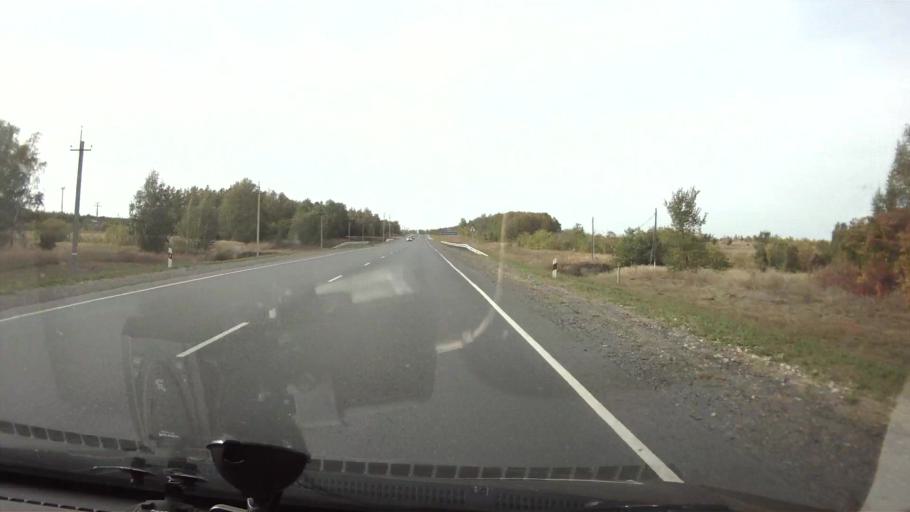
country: RU
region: Saratov
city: Shikhany
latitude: 52.1546
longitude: 47.1816
